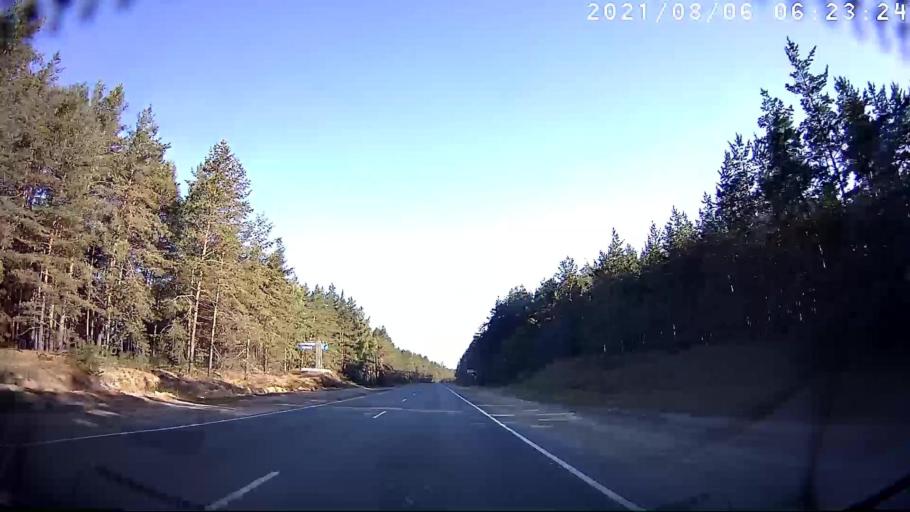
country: RU
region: Mariy-El
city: Krasnogorskiy
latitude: 56.0943
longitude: 48.3469
